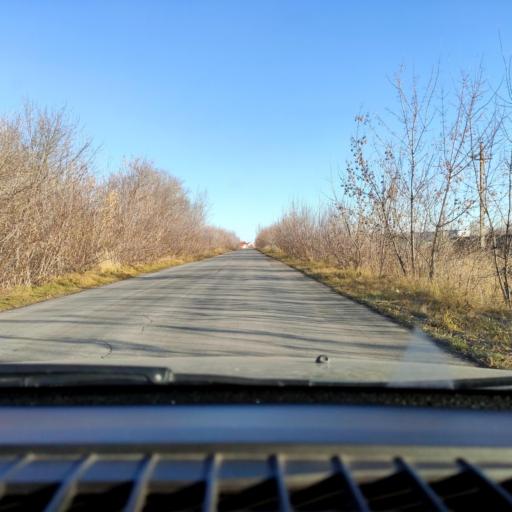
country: RU
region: Samara
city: Tol'yatti
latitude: 53.6615
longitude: 49.3345
